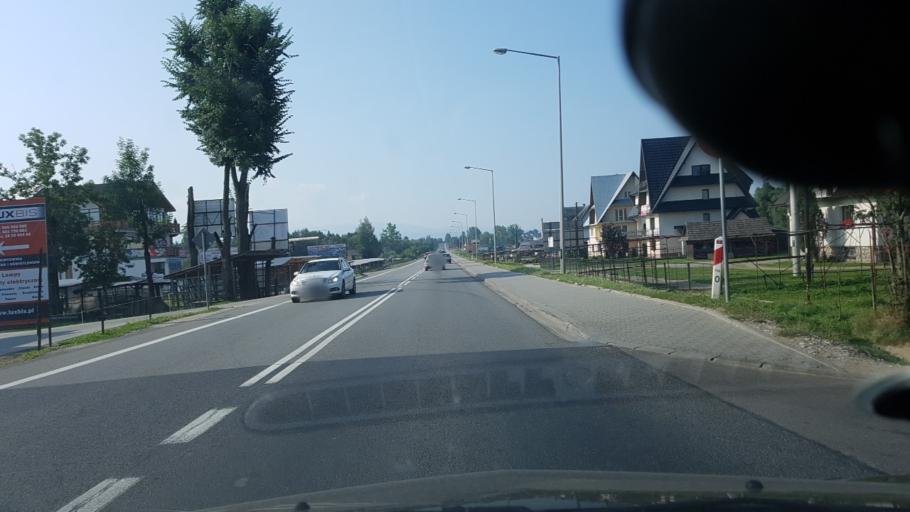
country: PL
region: Lesser Poland Voivodeship
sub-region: Powiat nowotarski
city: Jablonka
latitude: 49.4725
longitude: 19.6926
